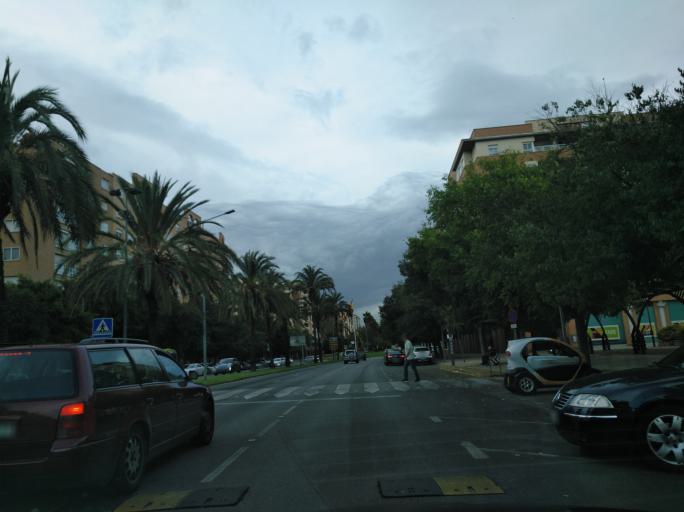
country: ES
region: Extremadura
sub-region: Provincia de Badajoz
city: Badajoz
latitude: 38.8679
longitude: -6.9869
